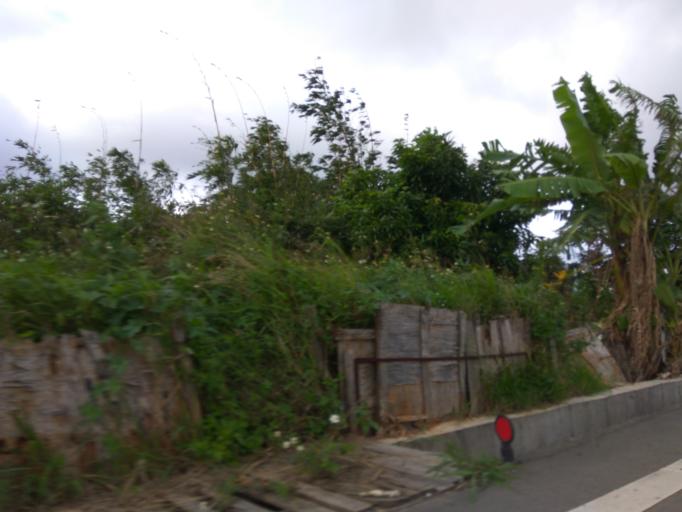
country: TW
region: Taiwan
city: Daxi
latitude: 24.9377
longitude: 121.1982
